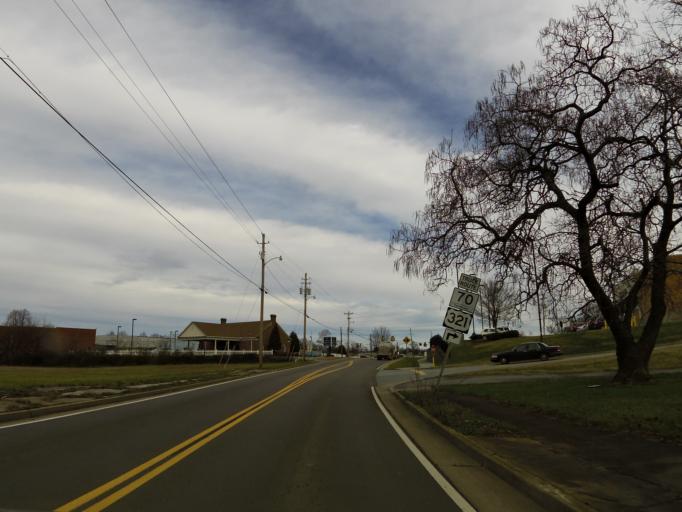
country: US
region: Tennessee
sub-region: Greene County
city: Greeneville
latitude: 36.1533
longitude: -82.8503
